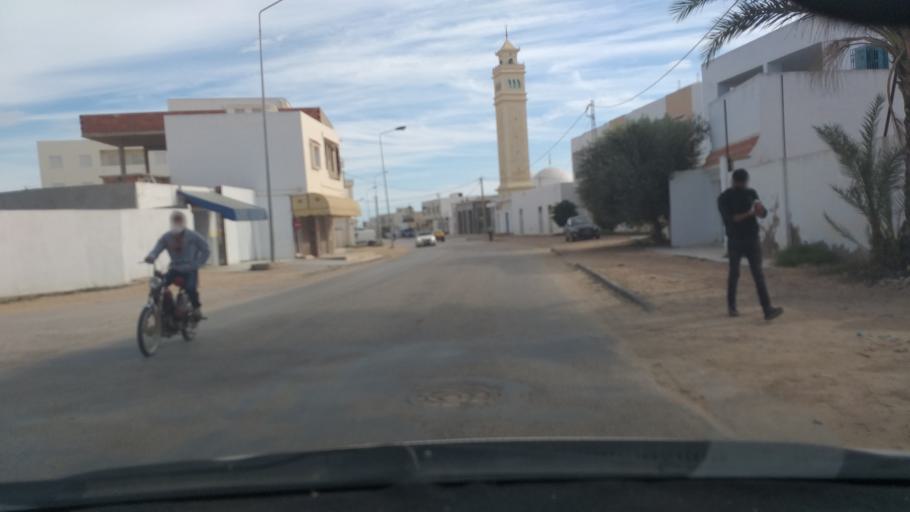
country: TN
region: Safaqis
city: Al Qarmadah
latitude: 34.7965
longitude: 10.8001
